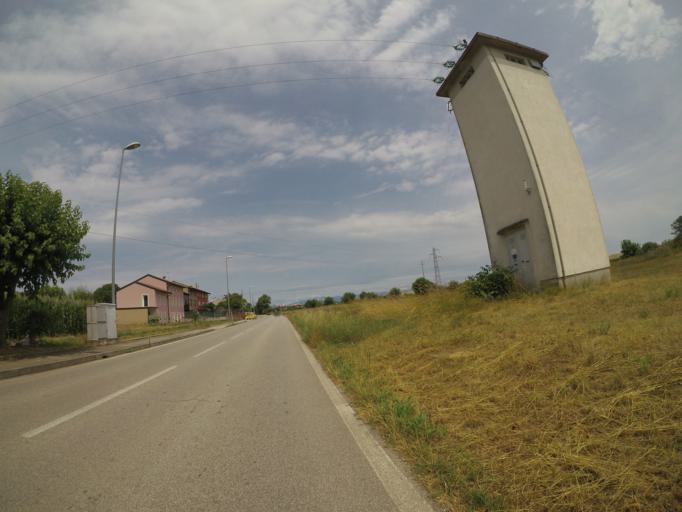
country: IT
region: Friuli Venezia Giulia
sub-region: Provincia di Udine
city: Sedegliano
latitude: 45.9947
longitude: 12.9987
